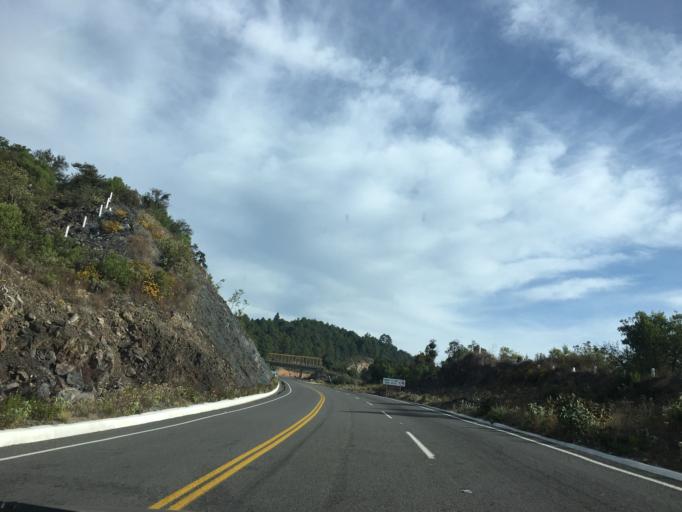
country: MX
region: Mexico
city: San Bartolo
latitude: 19.2604
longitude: -100.0653
